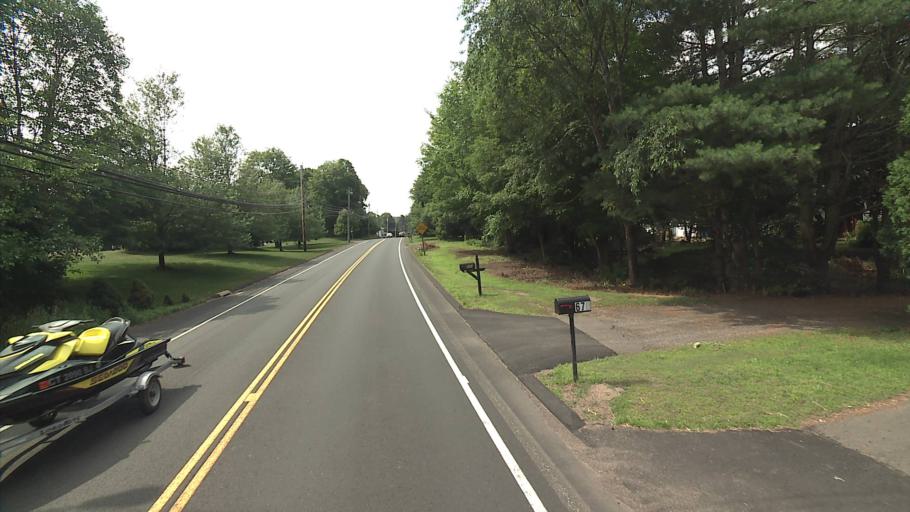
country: US
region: Connecticut
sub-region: New Haven County
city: North Branford
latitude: 41.3788
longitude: -72.7937
